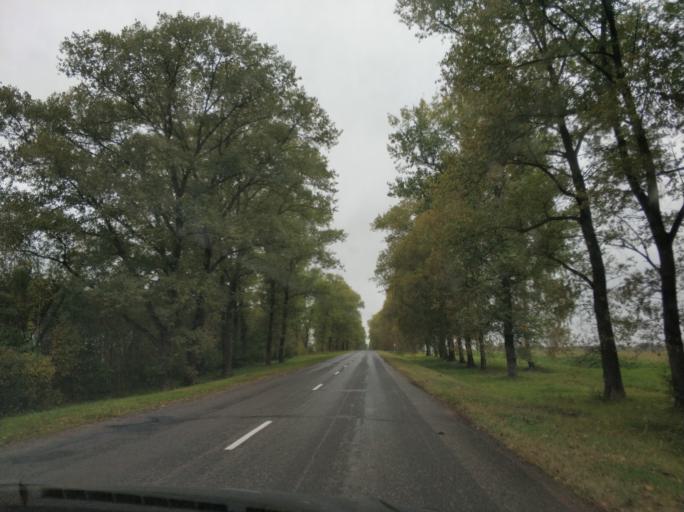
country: BY
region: Vitebsk
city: Polatsk
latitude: 55.4348
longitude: 28.9789
